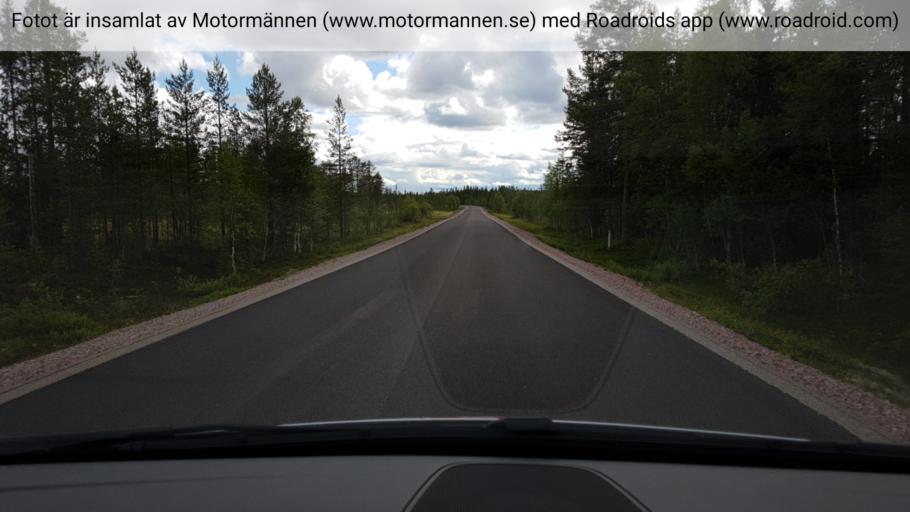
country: SE
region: Jaemtland
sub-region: Harjedalens Kommun
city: Sveg
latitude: 61.6576
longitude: 14.1760
